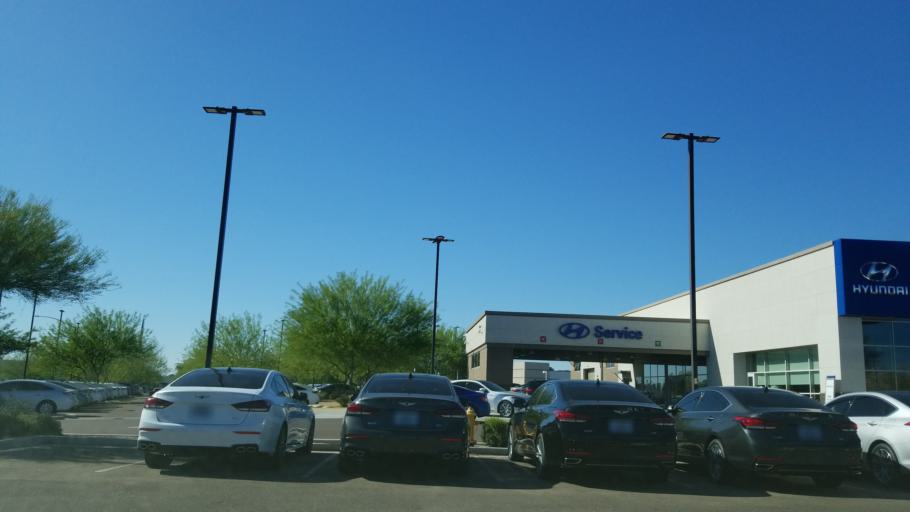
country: US
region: Arizona
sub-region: Maricopa County
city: Paradise Valley
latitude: 33.6317
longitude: -111.8982
